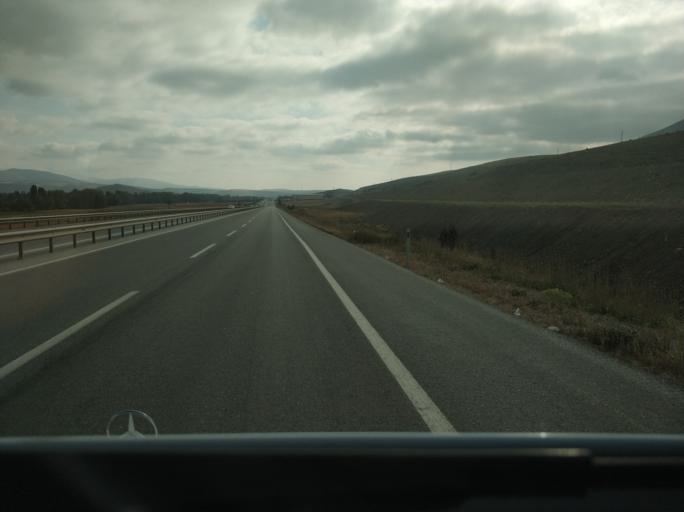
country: TR
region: Sivas
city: Yildizeli
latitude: 39.8578
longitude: 36.5558
